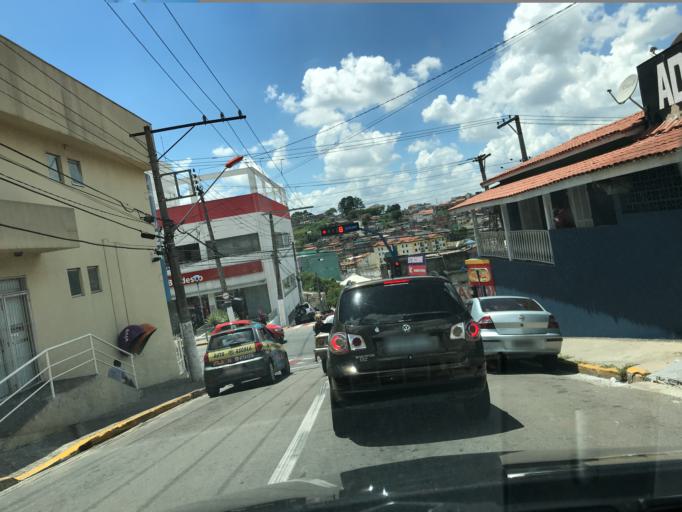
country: BR
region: Sao Paulo
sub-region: Itapevi
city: Itapevi
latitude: -23.5429
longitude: -46.9364
